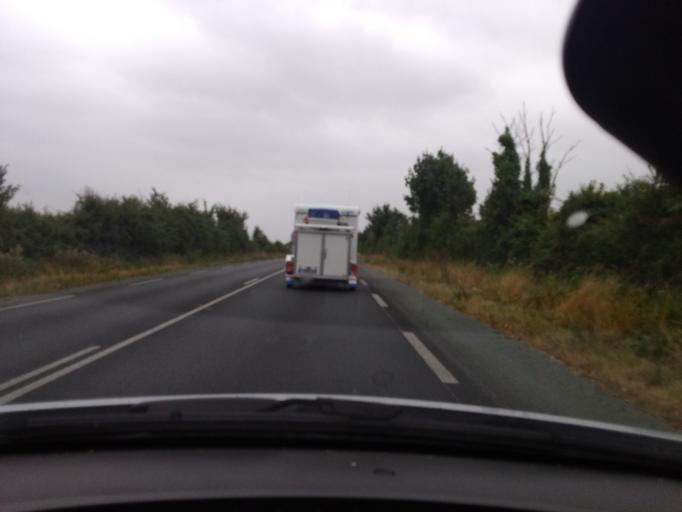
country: FR
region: Pays de la Loire
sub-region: Departement de la Vendee
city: Sainte-Gemme-la-Plaine
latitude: 46.5082
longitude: -1.0949
